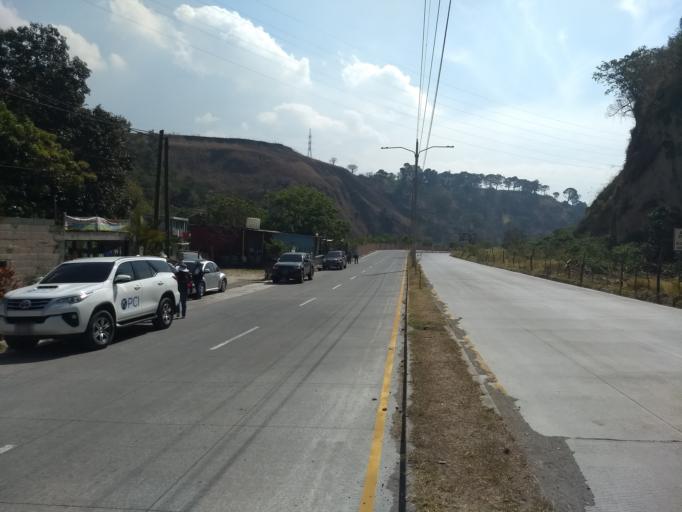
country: GT
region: Guatemala
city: Villa Nueva
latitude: 14.5524
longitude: -90.5909
